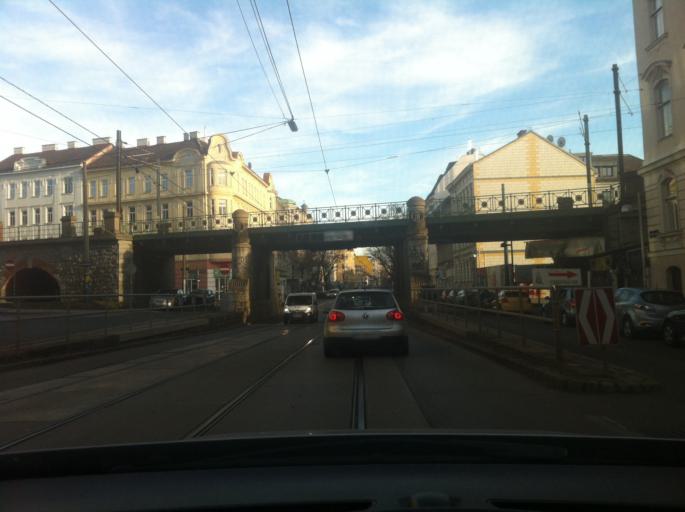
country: AT
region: Vienna
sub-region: Wien Stadt
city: Vienna
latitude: 48.1937
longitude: 16.3082
